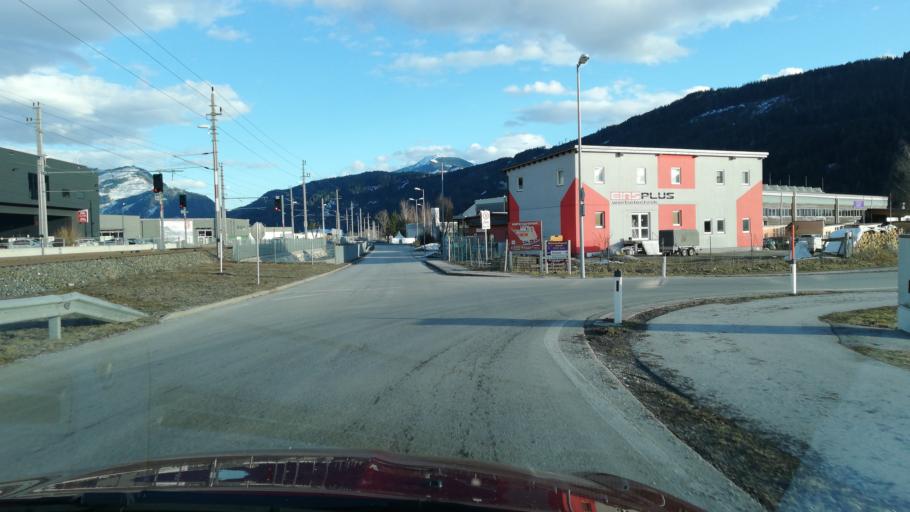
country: AT
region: Styria
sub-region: Politischer Bezirk Liezen
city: Liezen
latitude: 47.5613
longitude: 14.2441
